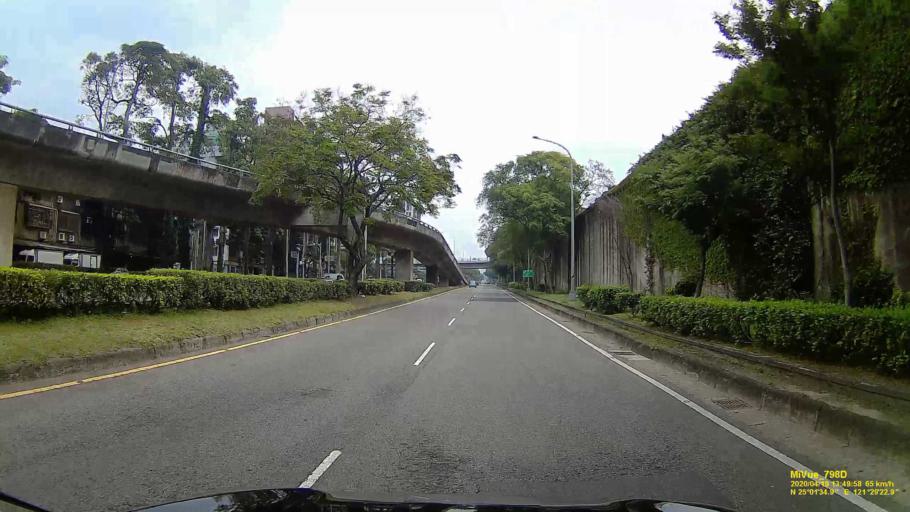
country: TW
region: Taipei
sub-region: Taipei
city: Banqiao
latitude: 25.0259
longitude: 121.4899
